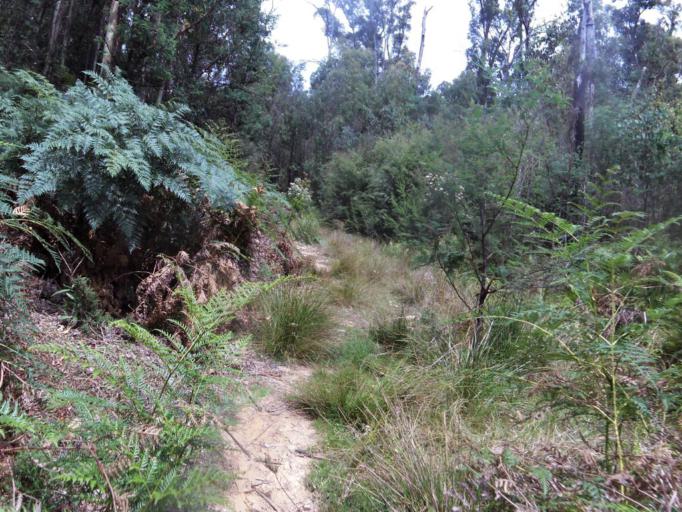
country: AU
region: Victoria
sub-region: Yarra Ranges
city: Healesville
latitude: -37.4402
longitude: 145.5786
